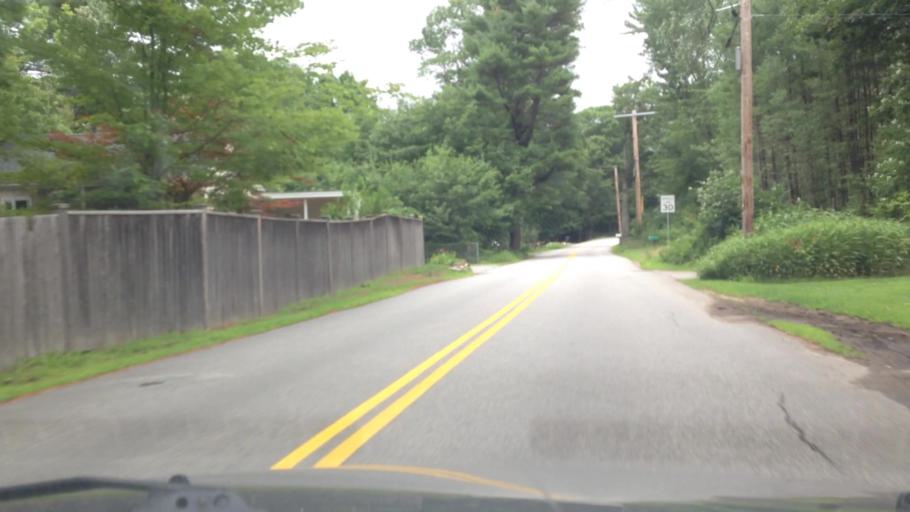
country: US
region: New Hampshire
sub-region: Cheshire County
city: Keene
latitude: 42.9114
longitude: -72.2541
